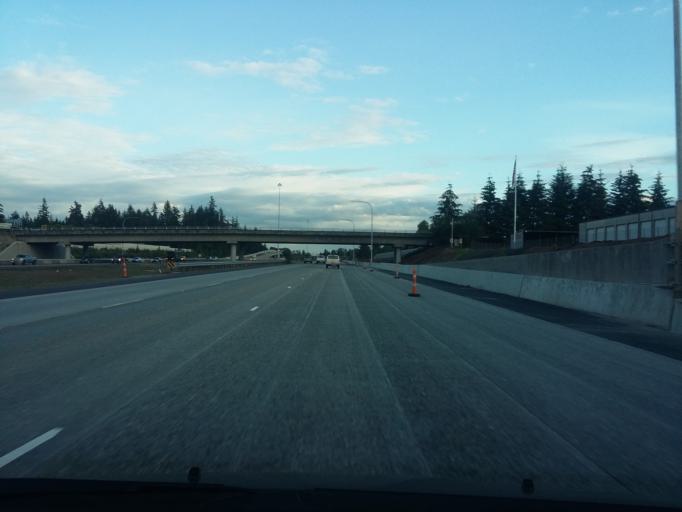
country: US
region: Washington
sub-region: Clark County
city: Orchards
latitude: 45.6298
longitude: -122.5600
